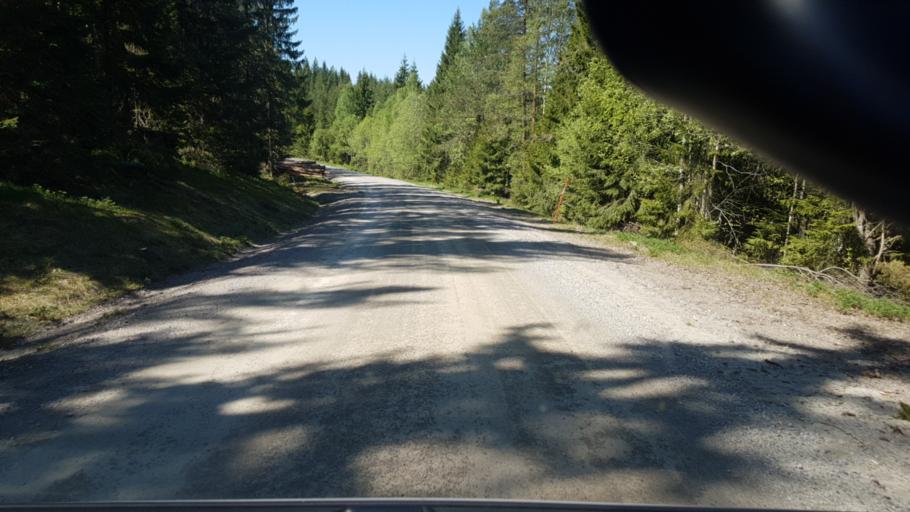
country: SE
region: Vaermland
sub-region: Arvika Kommun
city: Arvika
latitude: 59.8858
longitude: 12.6692
